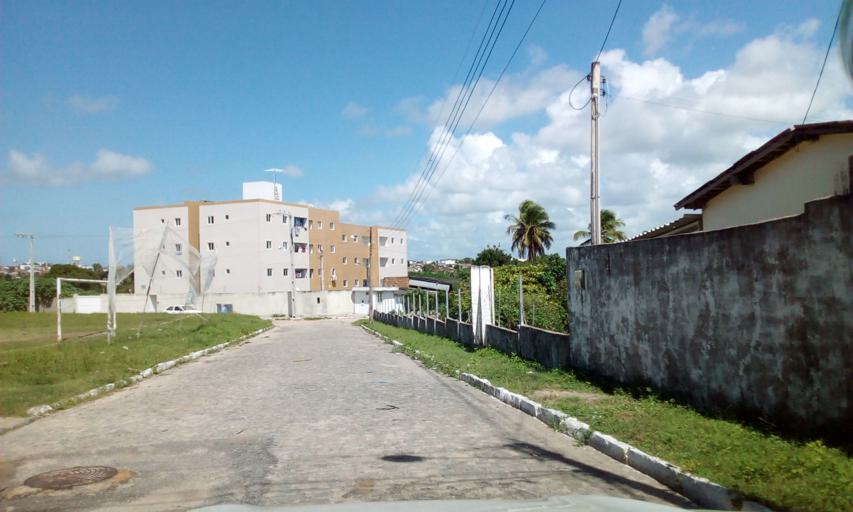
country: BR
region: Paraiba
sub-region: Joao Pessoa
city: Joao Pessoa
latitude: -7.1870
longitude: -34.8482
